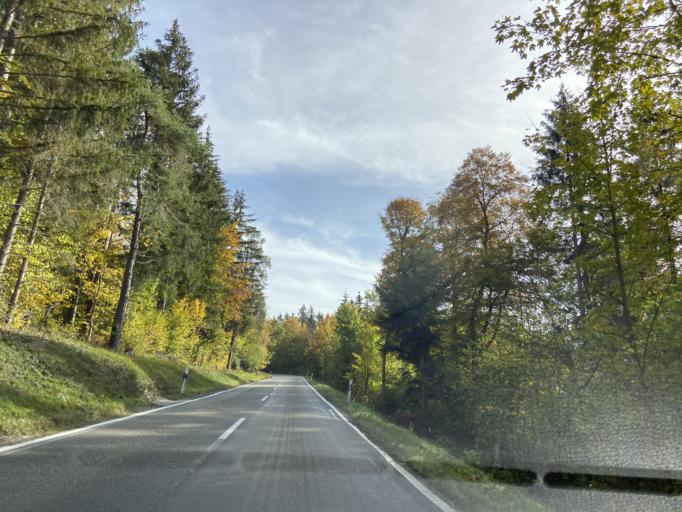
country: DE
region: Baden-Wuerttemberg
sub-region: Tuebingen Region
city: Schwenningen
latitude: 48.1146
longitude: 9.0230
